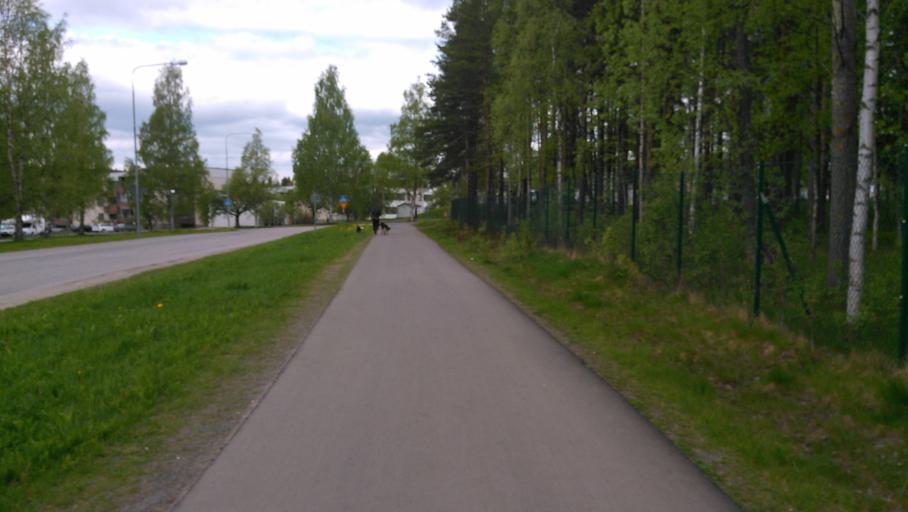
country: SE
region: Vaesterbotten
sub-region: Umea Kommun
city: Ersmark
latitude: 63.8308
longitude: 20.3231
